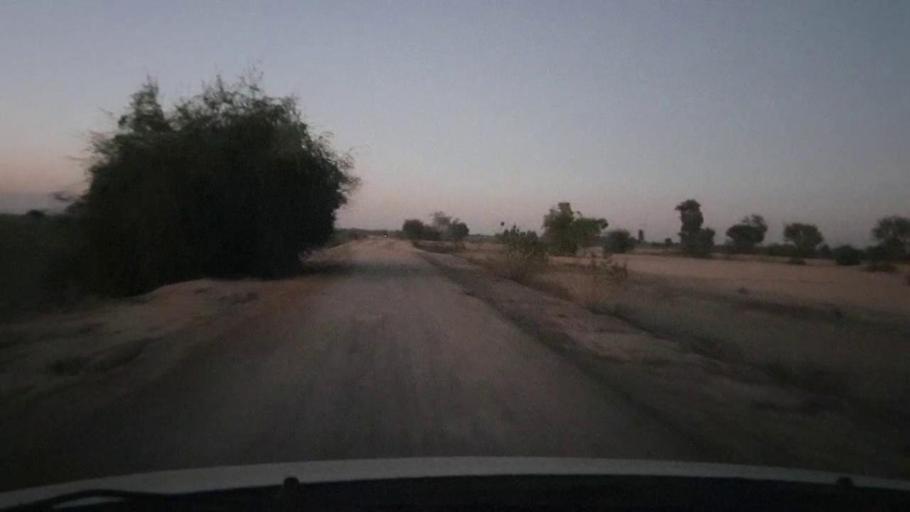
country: PK
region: Sindh
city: Phulji
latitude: 26.9047
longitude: 67.4707
